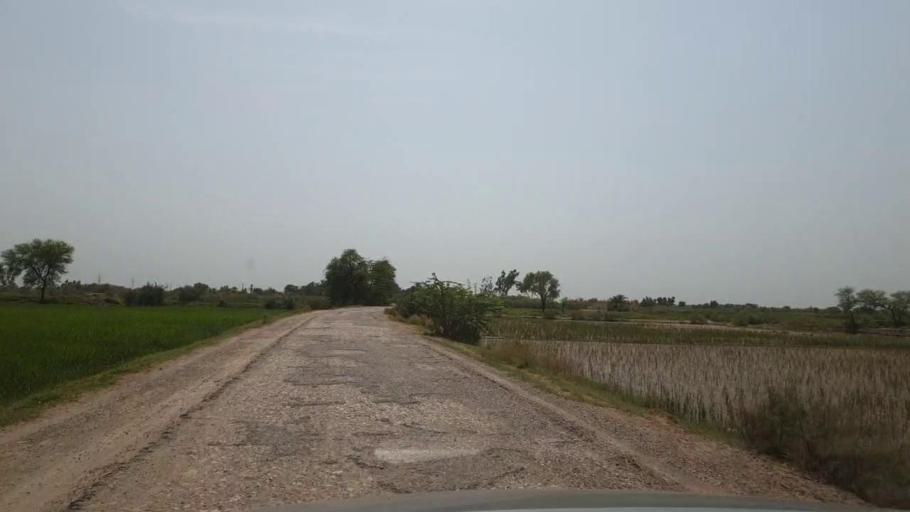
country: PK
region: Sindh
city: Garhi Yasin
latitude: 27.8925
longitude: 68.4687
